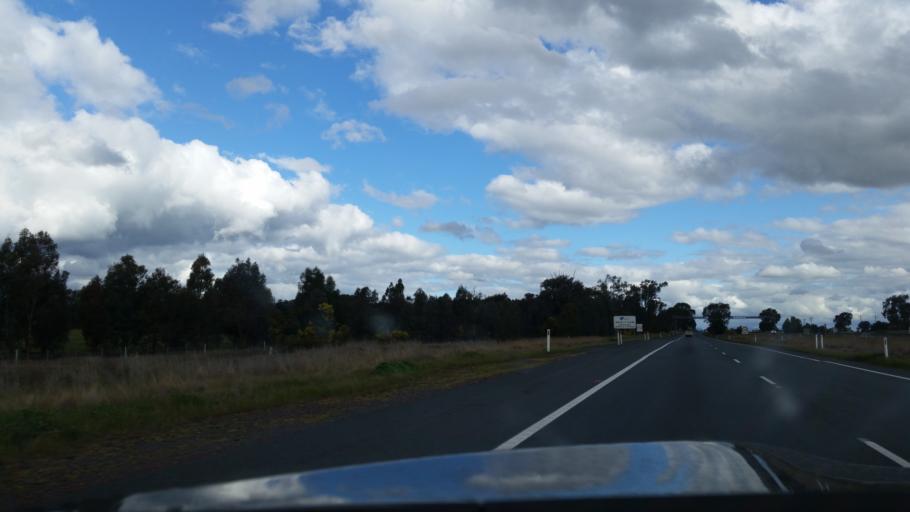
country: AU
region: New South Wales
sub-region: Albury Municipality
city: Lavington
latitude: -35.9643
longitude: 147.0050
